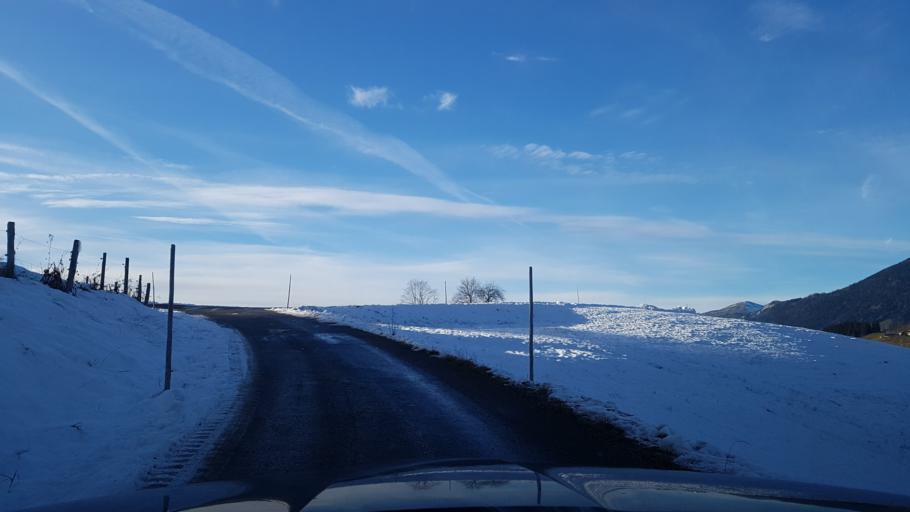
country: AT
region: Salzburg
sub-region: Politischer Bezirk Hallein
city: Abtenau
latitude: 47.5735
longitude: 13.4132
